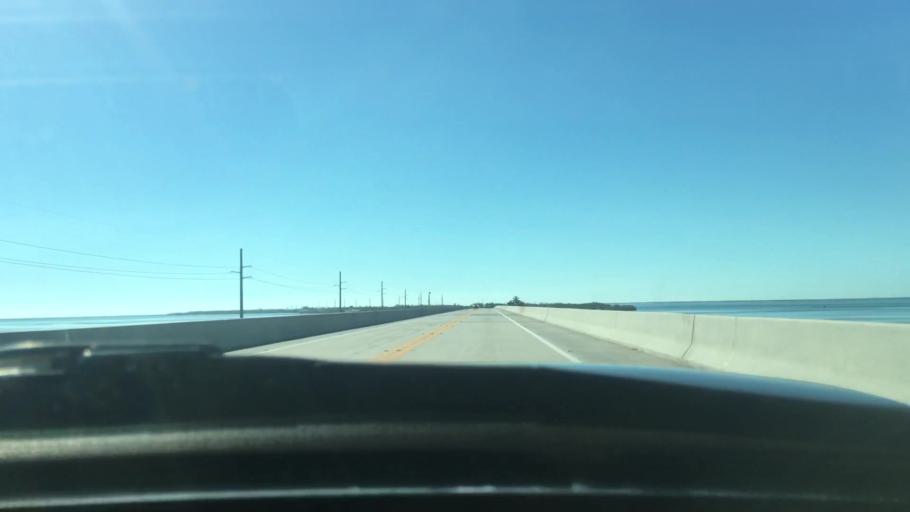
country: US
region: Florida
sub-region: Monroe County
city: Big Pine Key
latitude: 24.6849
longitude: -81.2227
